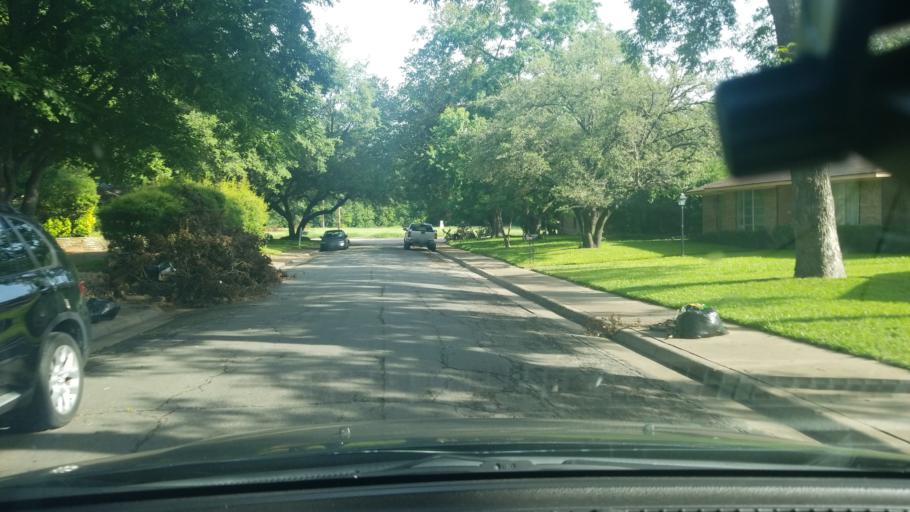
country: US
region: Texas
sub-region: Dallas County
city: Highland Park
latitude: 32.8075
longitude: -96.7095
